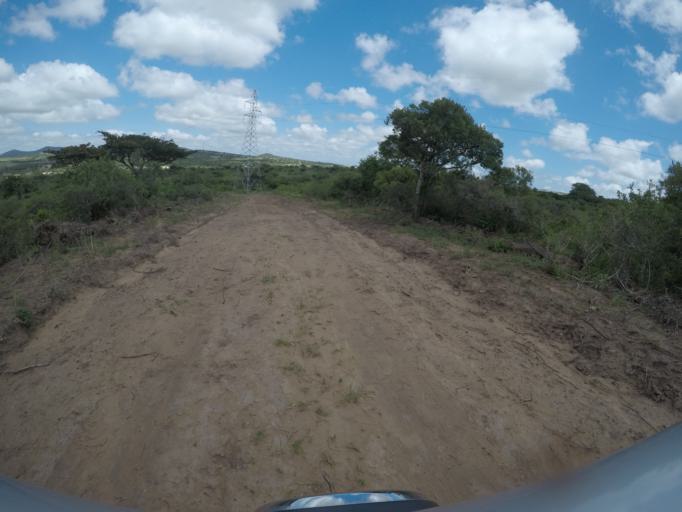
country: ZA
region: KwaZulu-Natal
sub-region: uThungulu District Municipality
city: Empangeni
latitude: -28.5858
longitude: 31.8360
